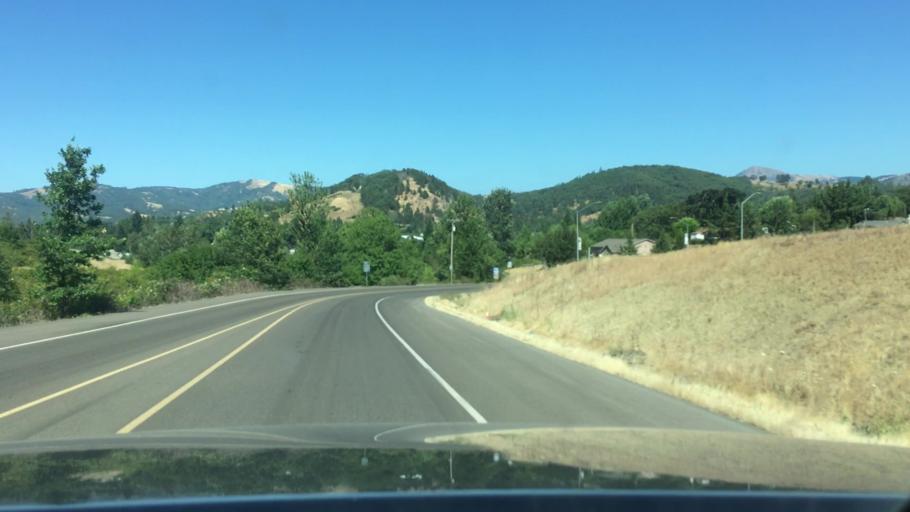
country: US
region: Oregon
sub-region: Douglas County
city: Winston
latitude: 43.1286
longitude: -123.4105
